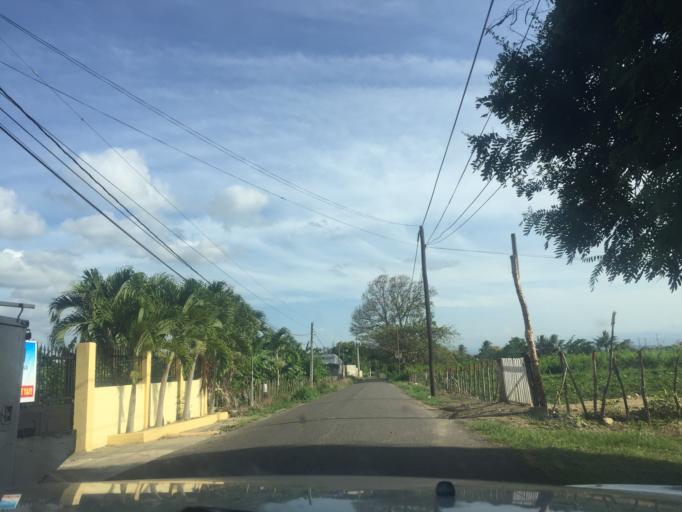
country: DO
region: Santiago
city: Tamboril
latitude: 19.4854
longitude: -70.6370
